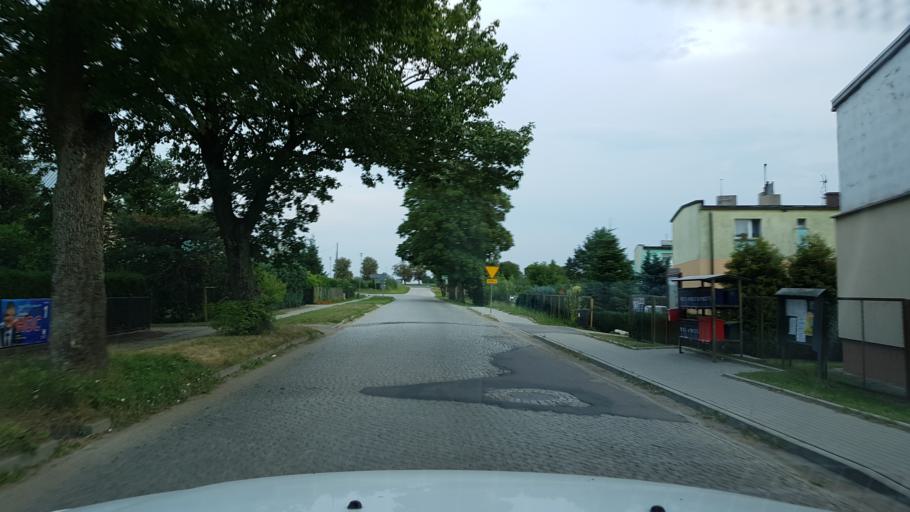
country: PL
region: West Pomeranian Voivodeship
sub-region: Powiat koszalinski
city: Mielno
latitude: 54.2239
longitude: 16.0252
